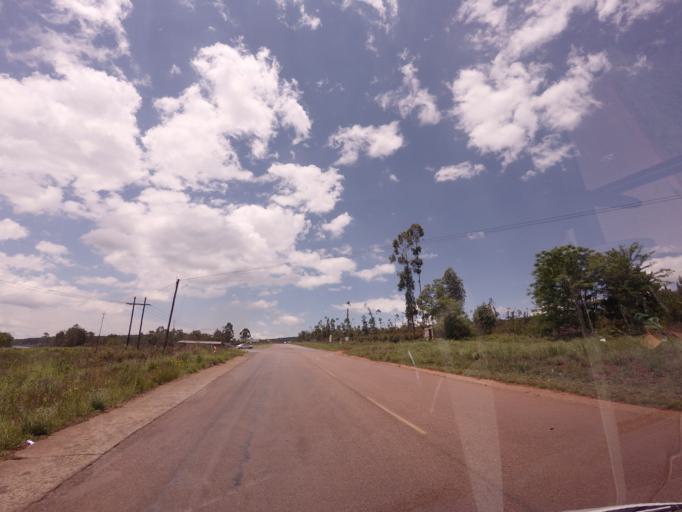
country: ZA
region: Mpumalanga
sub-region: Ehlanzeni District
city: Graksop
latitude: -25.0832
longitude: 30.7884
